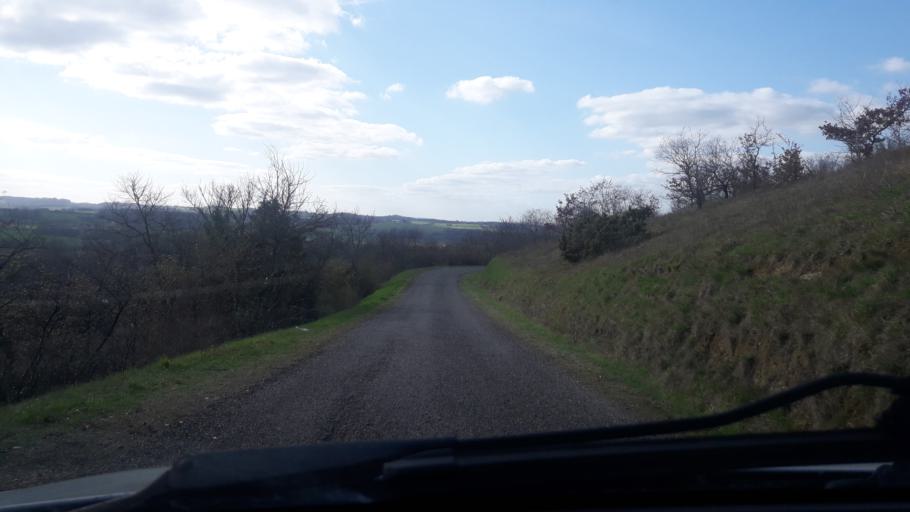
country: FR
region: Midi-Pyrenees
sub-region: Departement de la Haute-Garonne
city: Montesquieu-Volvestre
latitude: 43.2153
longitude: 1.2272
